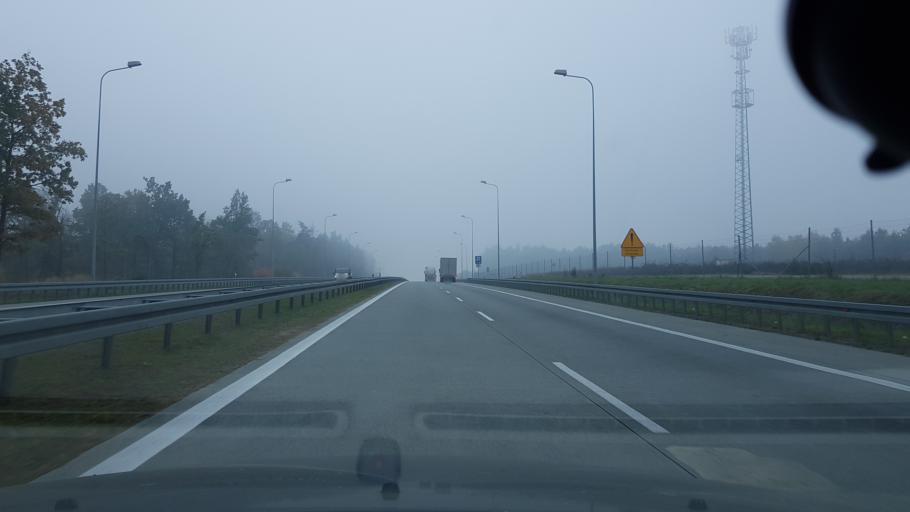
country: PL
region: Lodz Voivodeship
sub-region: Powiat rawski
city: Rawa Mazowiecka
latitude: 51.8220
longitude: 20.3199
